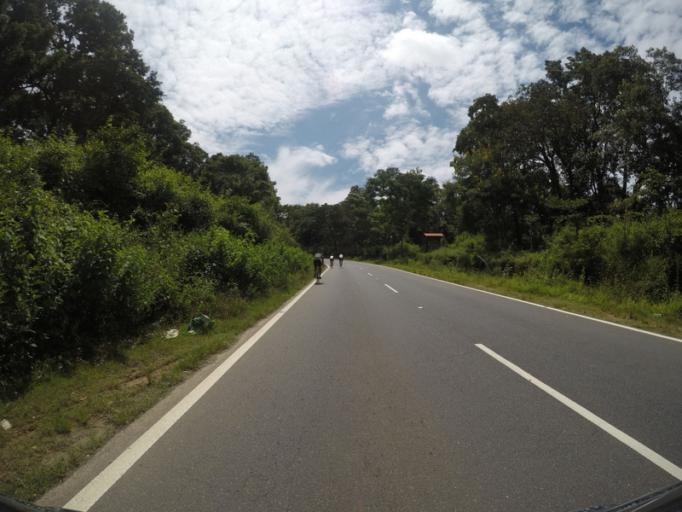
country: IN
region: Karnataka
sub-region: Kodagu
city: Suntikoppa
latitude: 12.4372
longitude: 75.8813
